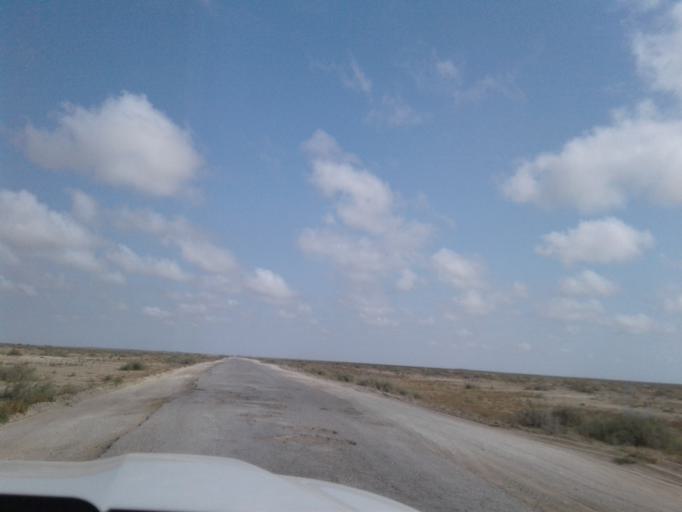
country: IR
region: Golestan
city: Gomishan
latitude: 37.5907
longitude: 53.9228
